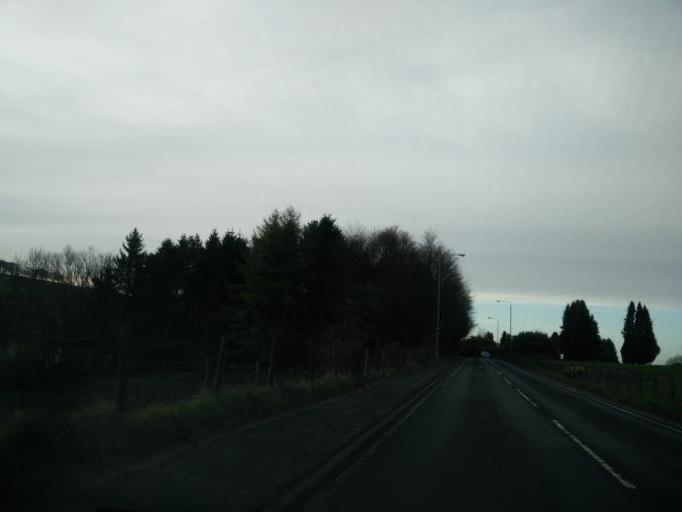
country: GB
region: England
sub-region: County Durham
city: Crook
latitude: 54.6992
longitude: -1.7494
